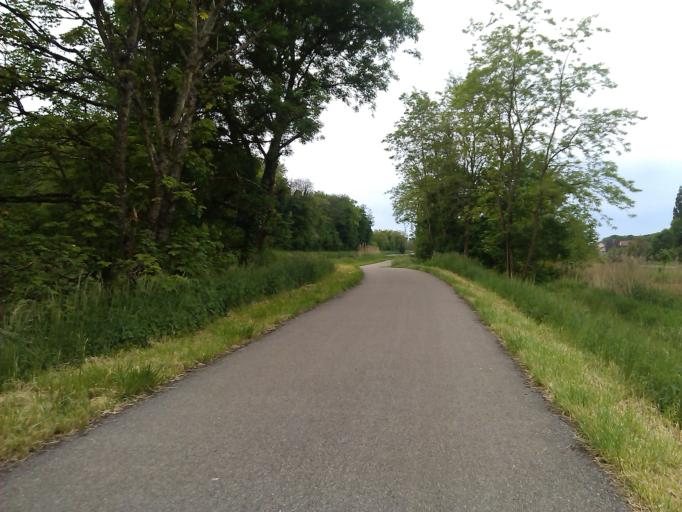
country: FR
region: Franche-Comte
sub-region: Departement du Jura
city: Choisey
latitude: 47.0683
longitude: 5.4665
